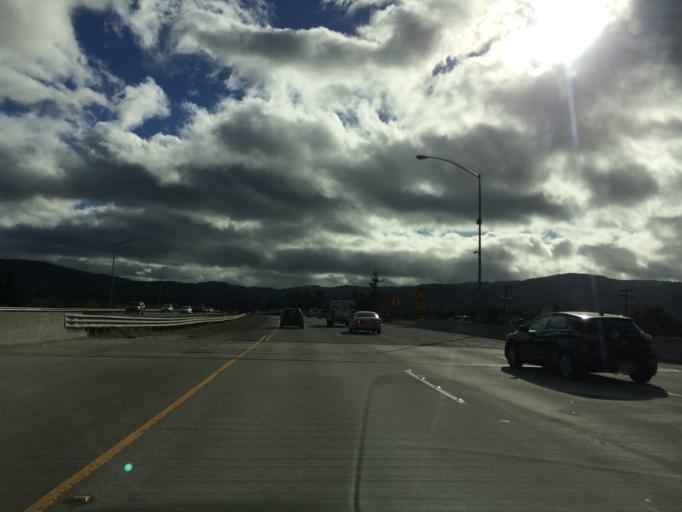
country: US
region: California
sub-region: Santa Clara County
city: Cambrian Park
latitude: 37.2556
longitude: -121.9562
